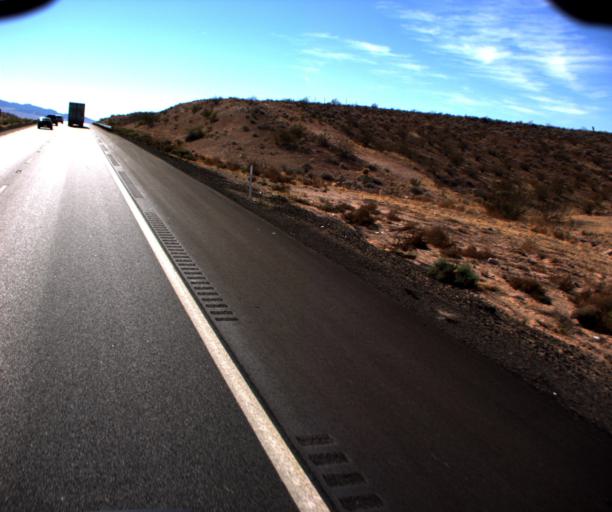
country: US
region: Arizona
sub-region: Mohave County
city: Beaver Dam
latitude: 36.8544
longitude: -113.9860
